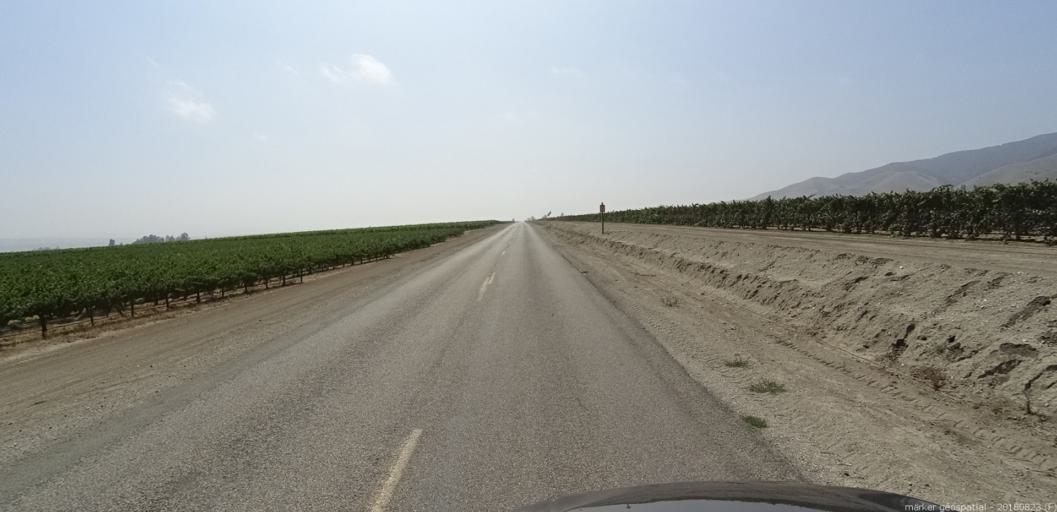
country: US
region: California
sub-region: Monterey County
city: Greenfield
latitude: 36.2687
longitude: -121.2173
